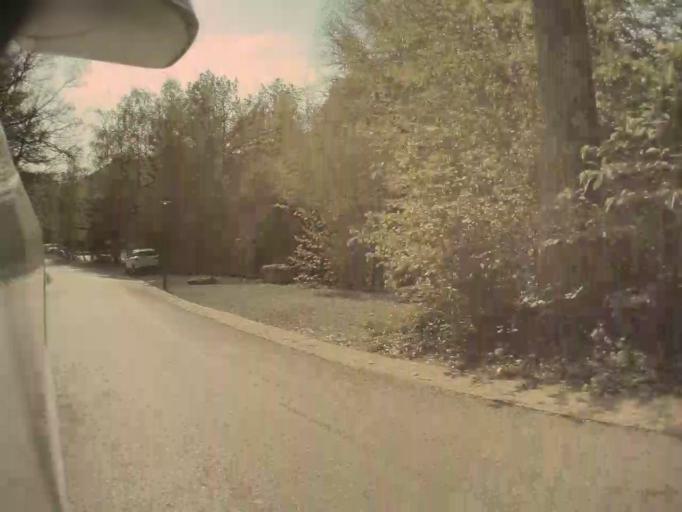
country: BE
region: Wallonia
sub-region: Province du Luxembourg
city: Durbuy
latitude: 50.3451
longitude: 5.4266
